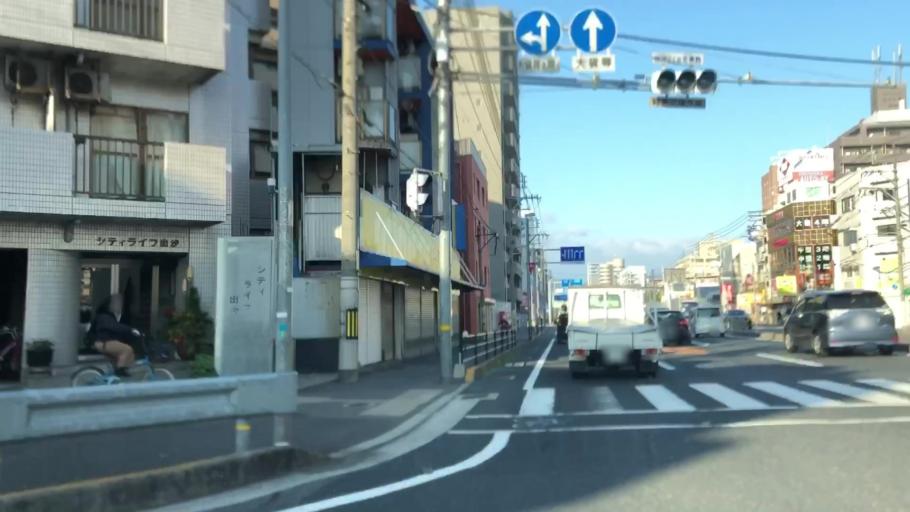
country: JP
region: Hiroshima
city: Hiroshima-shi
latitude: 34.3778
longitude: 132.4765
